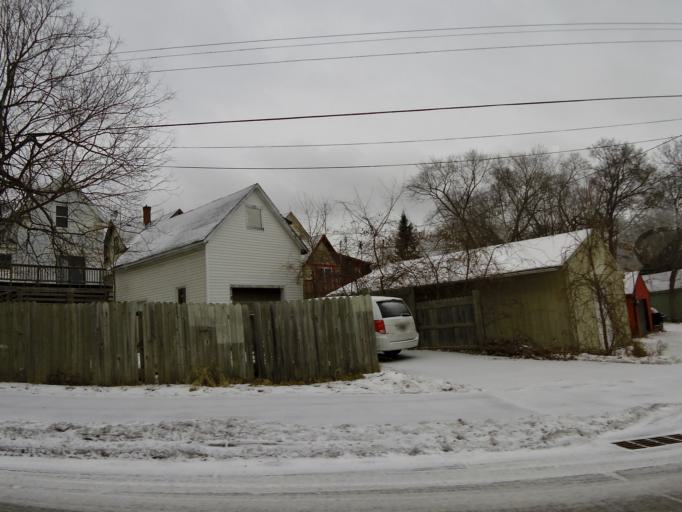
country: US
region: Minnesota
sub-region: Dakota County
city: West Saint Paul
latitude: 44.9197
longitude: -93.1320
